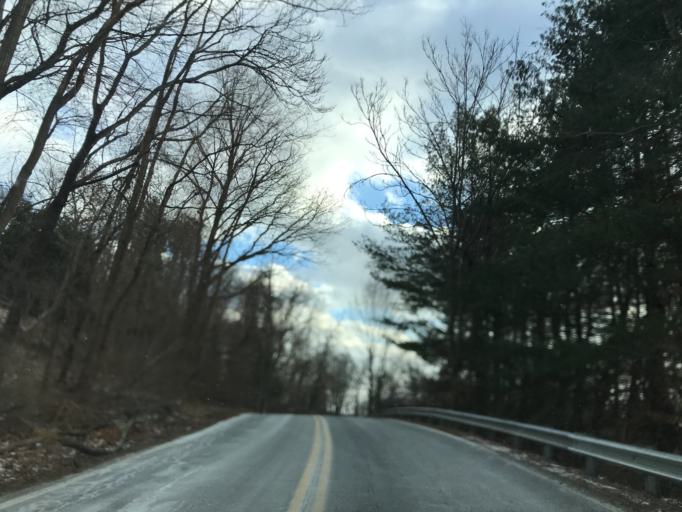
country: US
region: Maryland
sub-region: Harford County
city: Bel Air North
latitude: 39.6189
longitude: -76.3756
